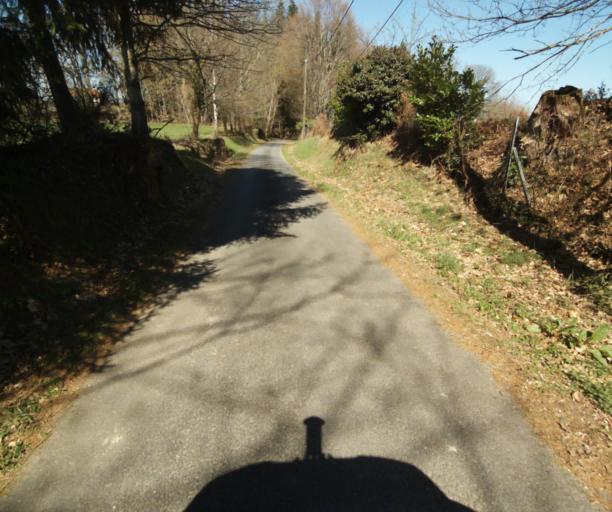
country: FR
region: Limousin
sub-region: Departement de la Correze
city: Chameyrat
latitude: 45.2743
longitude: 1.7043
